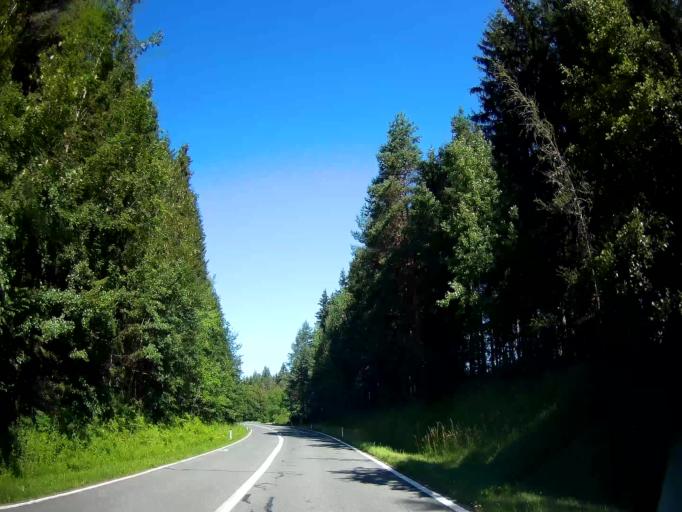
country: AT
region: Carinthia
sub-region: Politischer Bezirk Volkermarkt
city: Gallizien
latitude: 46.5505
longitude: 14.5105
